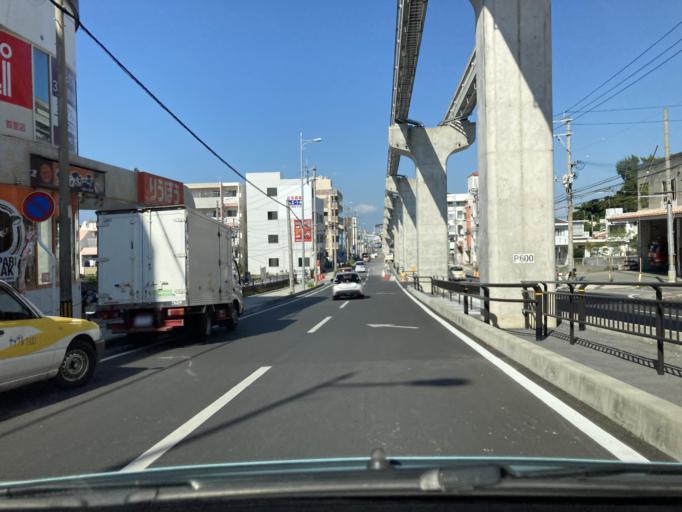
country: JP
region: Okinawa
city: Naha-shi
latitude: 26.2224
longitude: 127.7273
